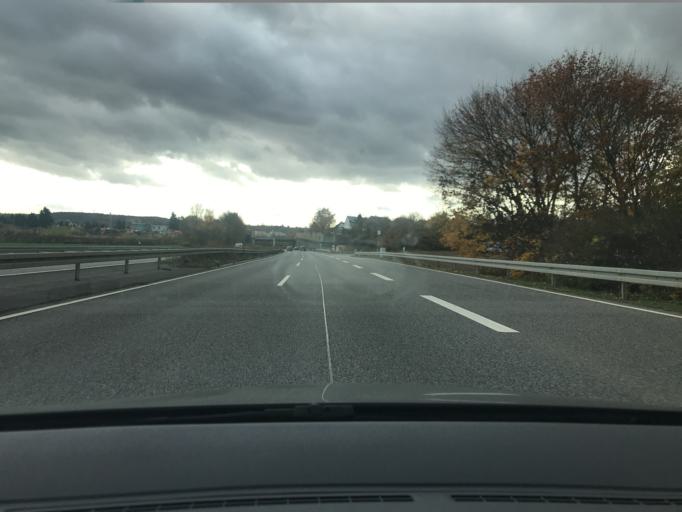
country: DE
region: Hesse
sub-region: Regierungsbezirk Darmstadt
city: Bad Vilbel
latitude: 50.1920
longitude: 8.7305
